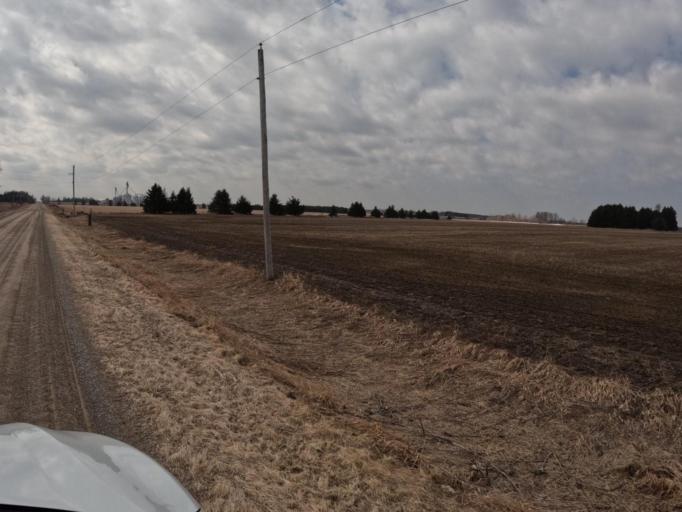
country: CA
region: Ontario
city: Orangeville
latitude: 43.9274
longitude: -80.2410
